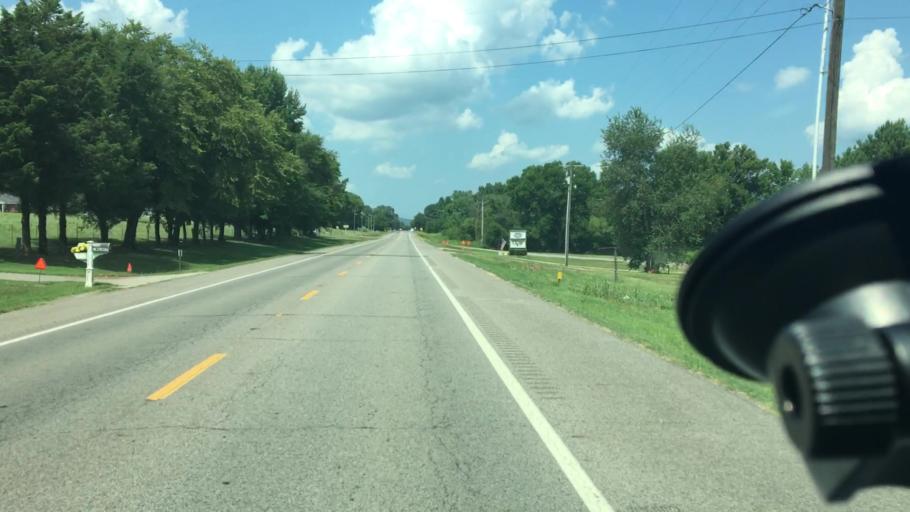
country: US
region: Arkansas
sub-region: Logan County
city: Paris
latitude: 35.2943
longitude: -93.6939
